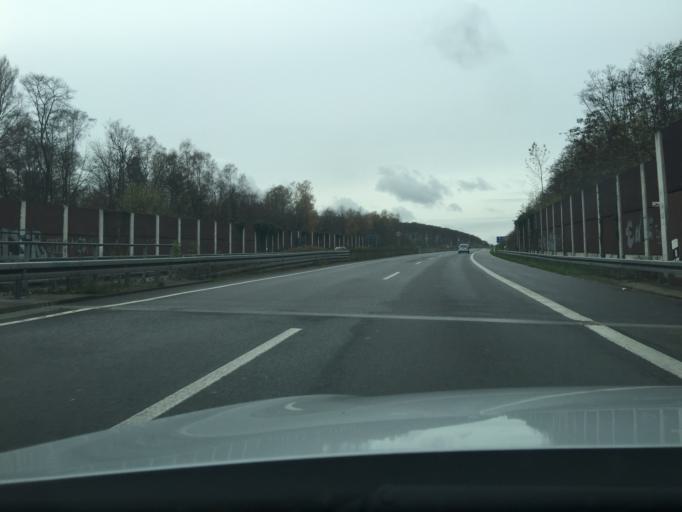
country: DE
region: North Rhine-Westphalia
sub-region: Regierungsbezirk Dusseldorf
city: Velbert
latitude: 51.3762
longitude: 7.0758
